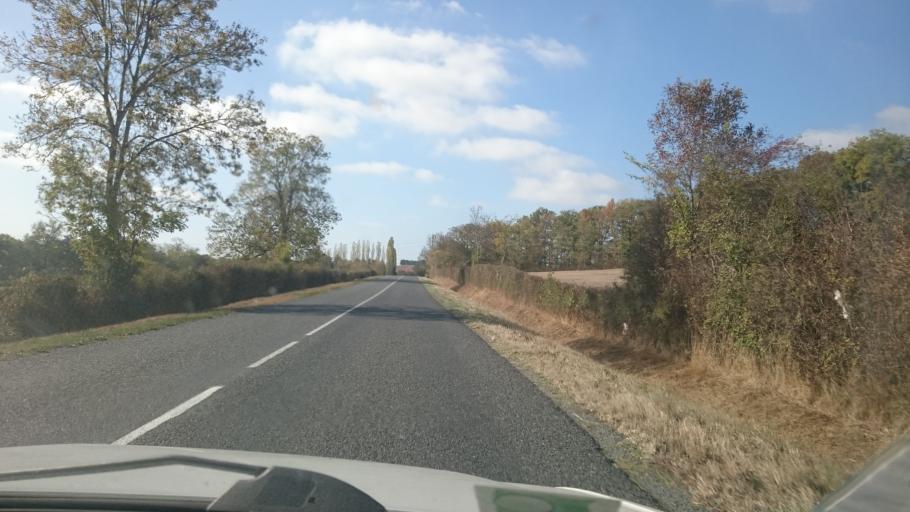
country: FR
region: Auvergne
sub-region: Departement de l'Allier
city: Souvigny
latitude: 46.5462
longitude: 3.2284
